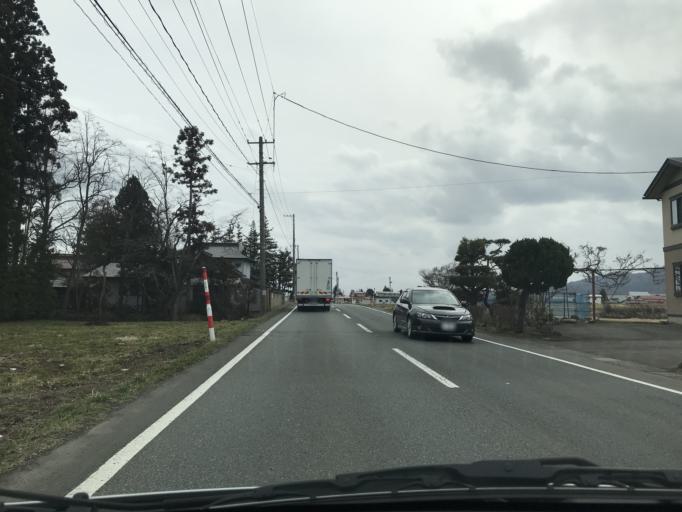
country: JP
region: Iwate
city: Morioka-shi
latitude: 39.5589
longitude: 141.1348
